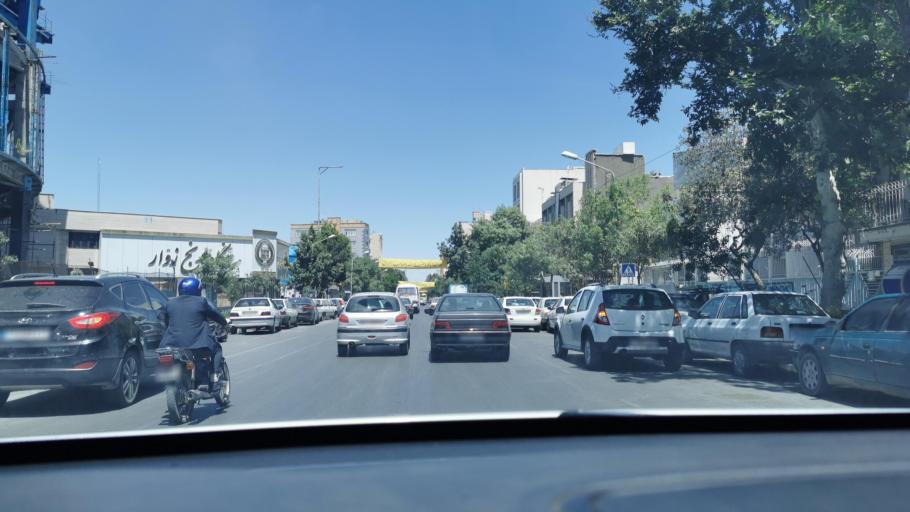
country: IR
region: Razavi Khorasan
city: Mashhad
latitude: 36.2996
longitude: 59.6103
